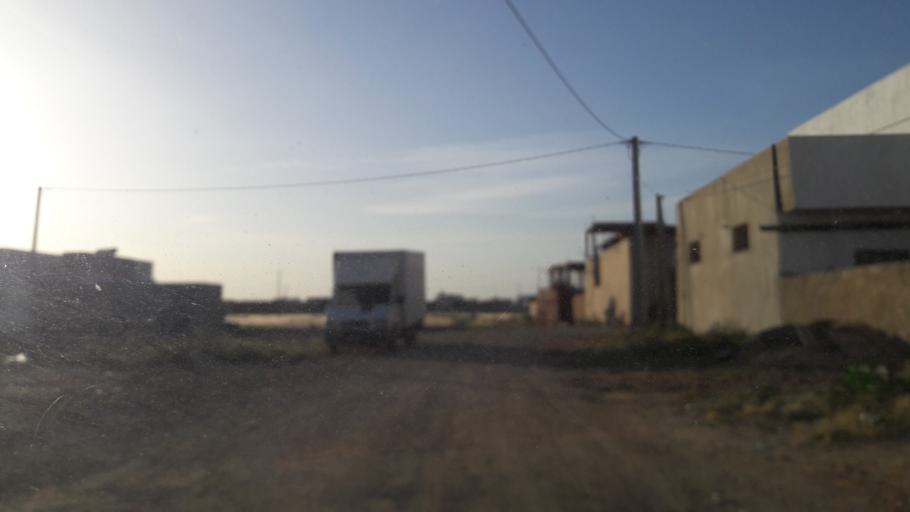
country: TN
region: Safaqis
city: Sfax
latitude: 34.8188
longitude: 10.7405
